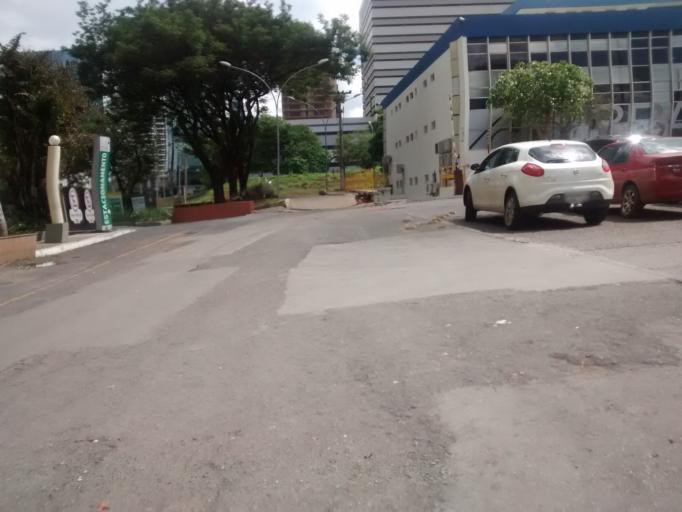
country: BR
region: Federal District
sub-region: Brasilia
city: Brasilia
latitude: -15.7869
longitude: -47.8848
